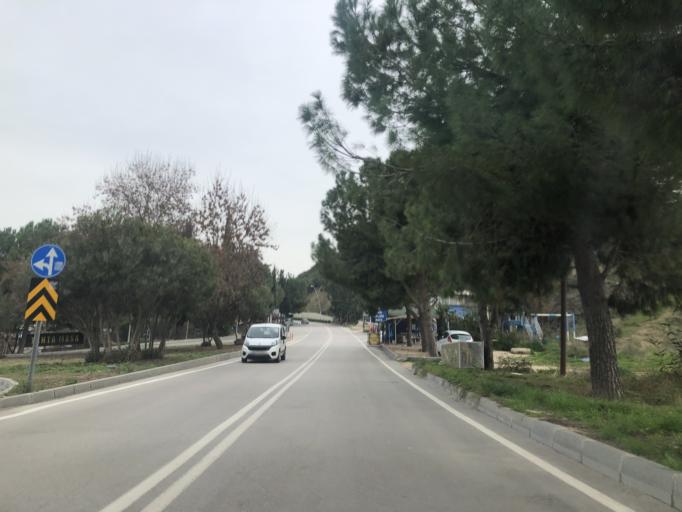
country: TR
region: Adana
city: Adana
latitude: 37.0593
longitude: 35.3002
